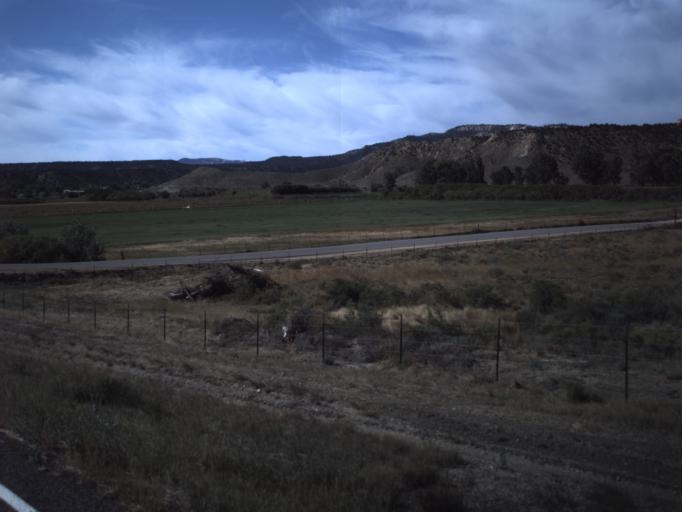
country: US
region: Utah
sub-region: Garfield County
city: Panguitch
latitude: 37.6407
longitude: -112.0816
